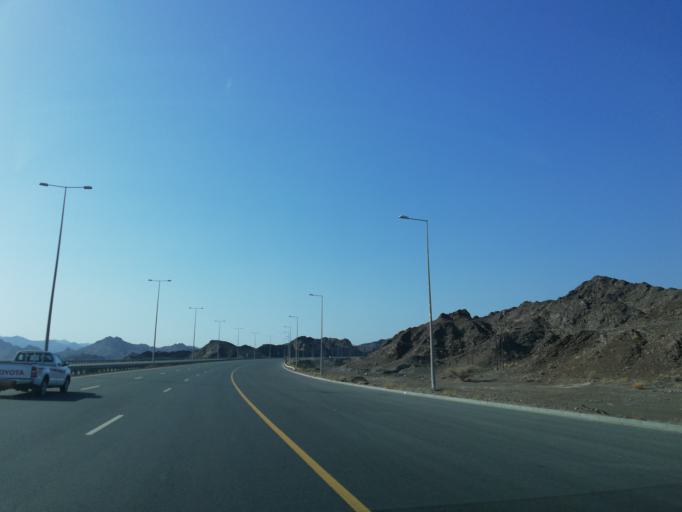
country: OM
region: Muhafazat ad Dakhiliyah
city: Sufalat Sama'il
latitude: 23.0061
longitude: 58.2279
